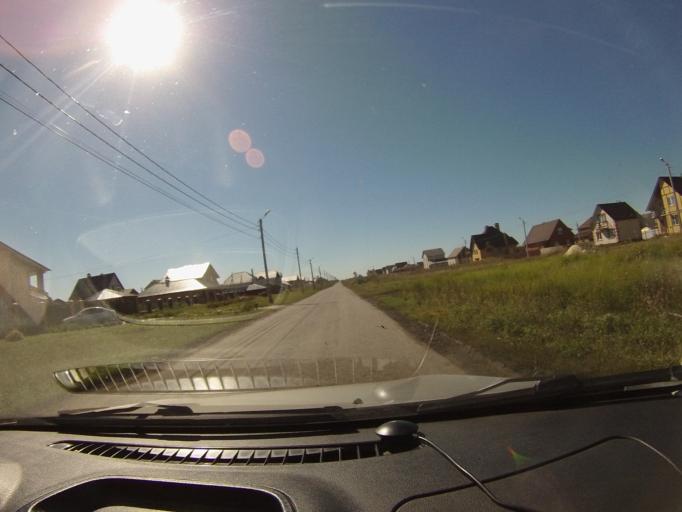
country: RU
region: Tambov
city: Komsomolets
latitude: 52.7765
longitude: 41.3699
